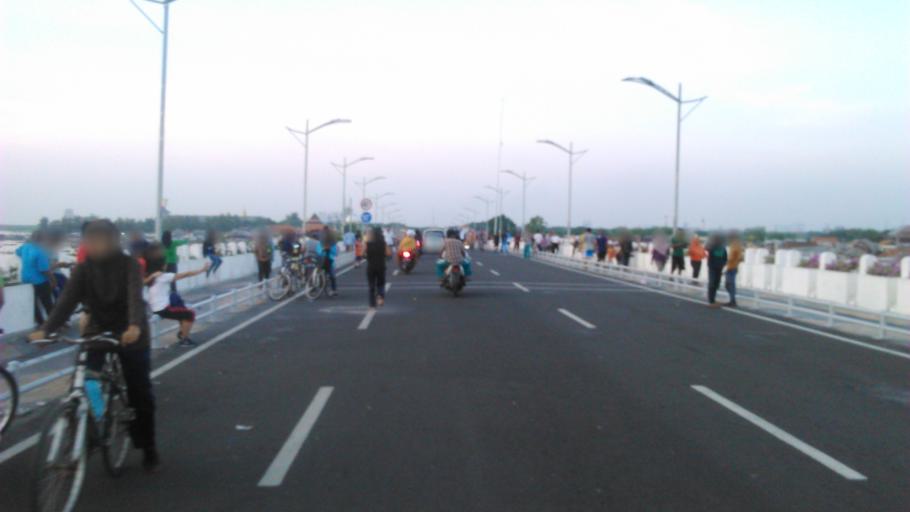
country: ID
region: East Java
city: Labansari
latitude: -7.2374
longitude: 112.7971
